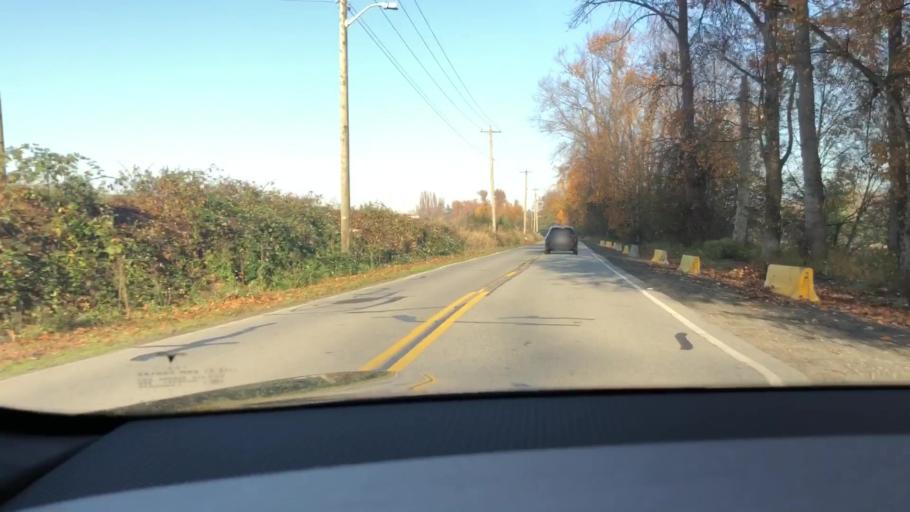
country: CA
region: British Columbia
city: New Westminster
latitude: 49.1881
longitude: -123.0004
